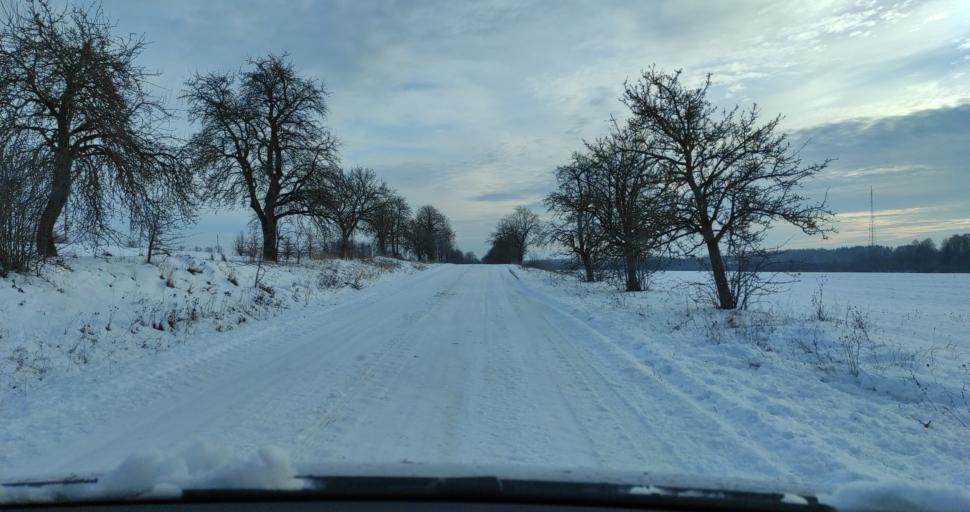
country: LV
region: Kuldigas Rajons
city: Kuldiga
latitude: 56.9542
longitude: 22.0157
